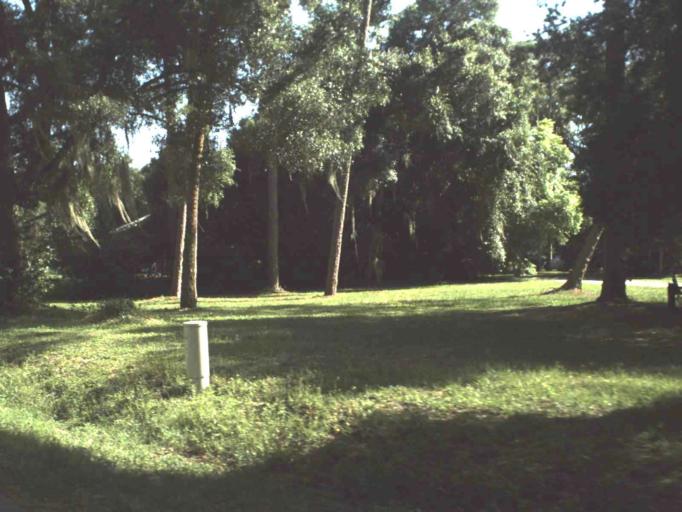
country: US
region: Florida
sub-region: Volusia County
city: Lake Helen
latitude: 29.0239
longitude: -81.2533
